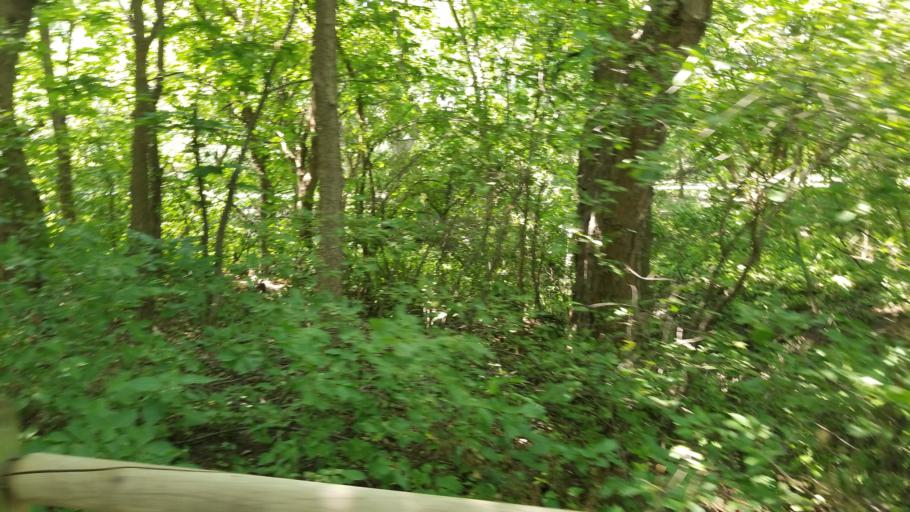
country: US
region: Nebraska
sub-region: Douglas County
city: Elkhorn
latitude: 41.2798
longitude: -96.1652
